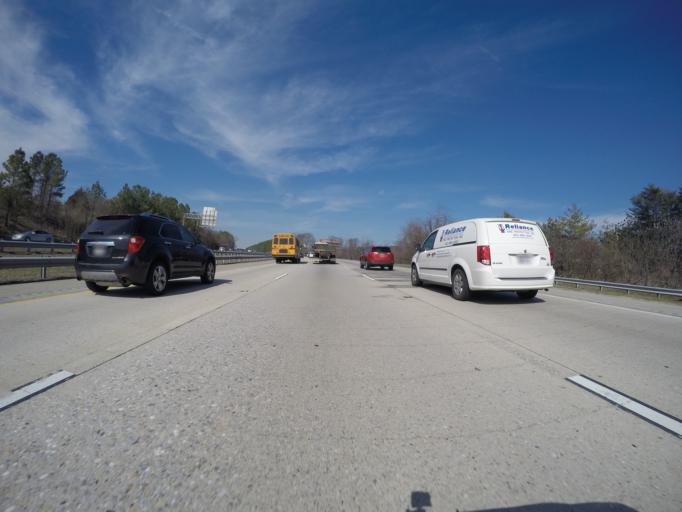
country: US
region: Maryland
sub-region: Anne Arundel County
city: Gambrills
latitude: 39.0836
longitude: -76.6253
